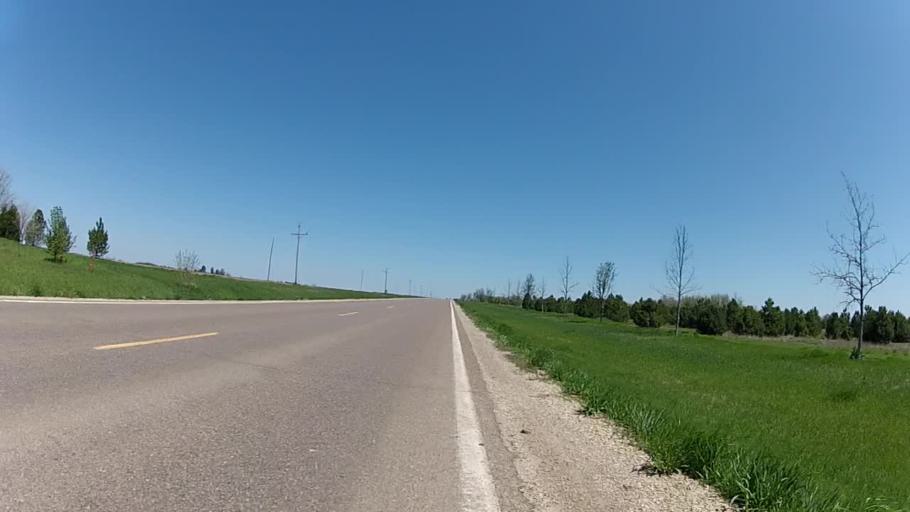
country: US
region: Kansas
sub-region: Riley County
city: Manhattan
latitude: 38.9574
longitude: -96.5201
